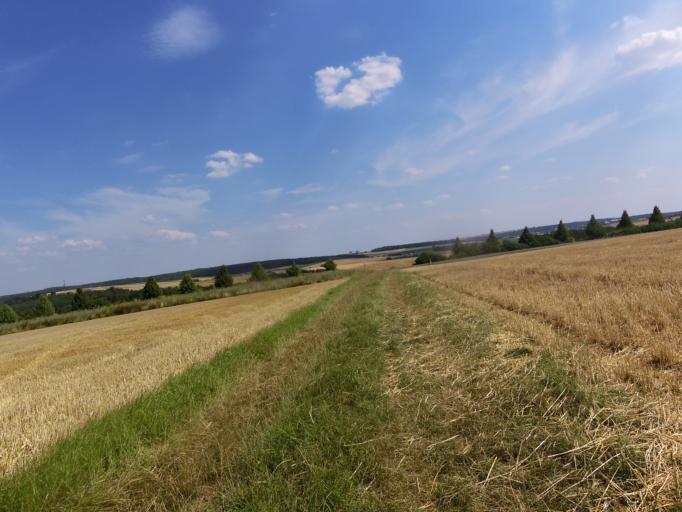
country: DE
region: Bavaria
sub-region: Regierungsbezirk Unterfranken
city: Estenfeld
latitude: 49.8222
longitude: 9.9916
